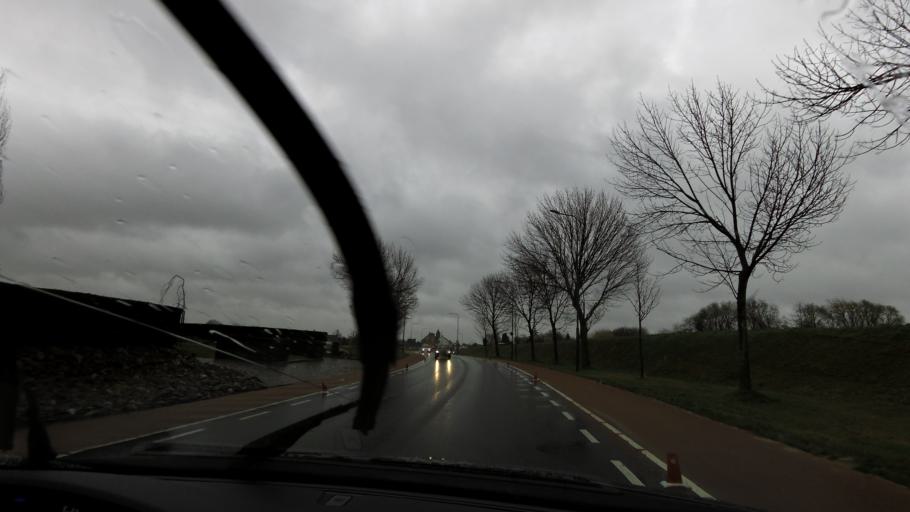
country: NL
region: Limburg
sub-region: Gemeente Sittard-Geleen
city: Limbricht
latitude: 51.0165
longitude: 5.8316
